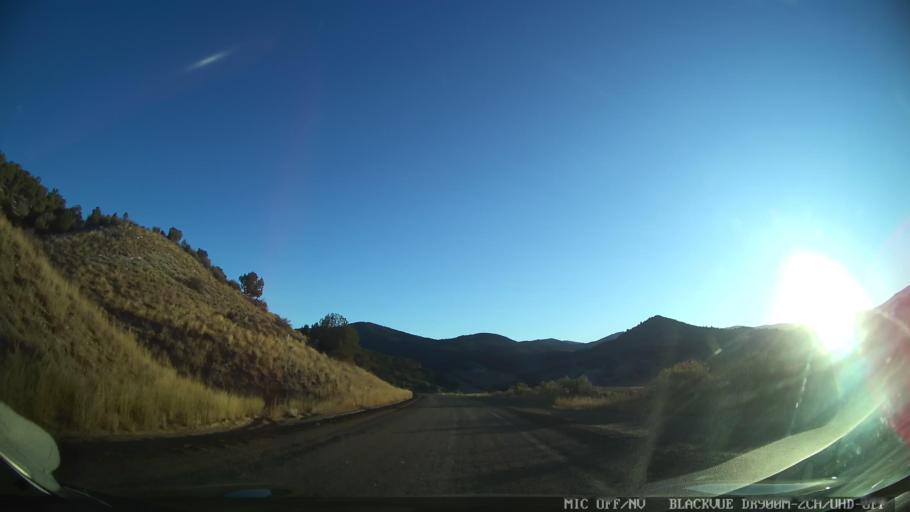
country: US
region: Colorado
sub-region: Grand County
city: Kremmling
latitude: 39.9237
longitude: -106.5367
